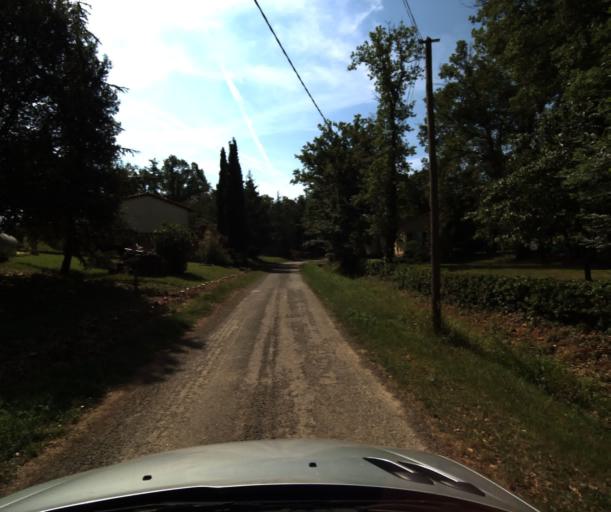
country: FR
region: Midi-Pyrenees
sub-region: Departement de la Haute-Garonne
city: Labastidette
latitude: 43.4684
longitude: 1.2097
